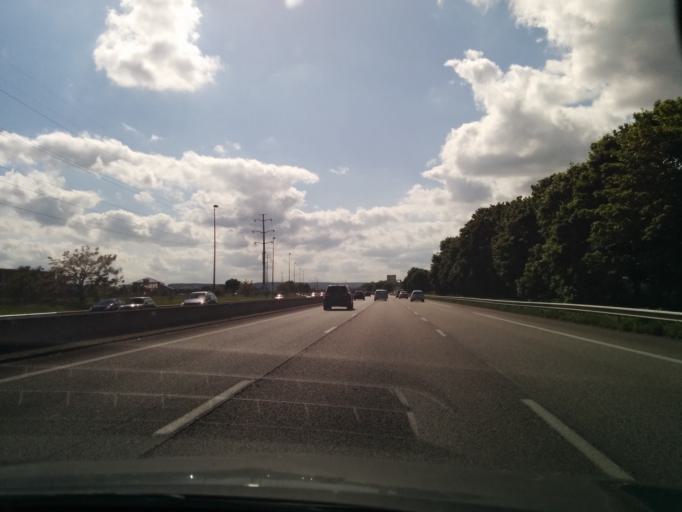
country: FR
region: Ile-de-France
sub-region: Departement des Yvelines
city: Flins-sur-Seine
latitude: 48.9705
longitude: 1.8740
